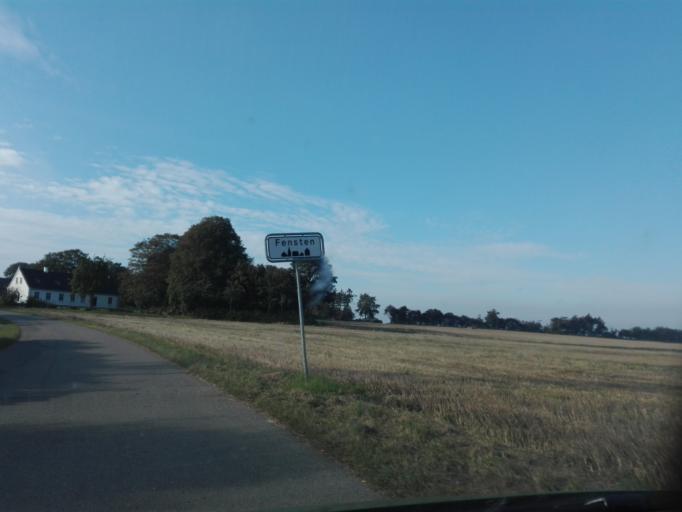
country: DK
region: Central Jutland
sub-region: Odder Kommune
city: Odder
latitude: 55.9042
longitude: 10.1909
